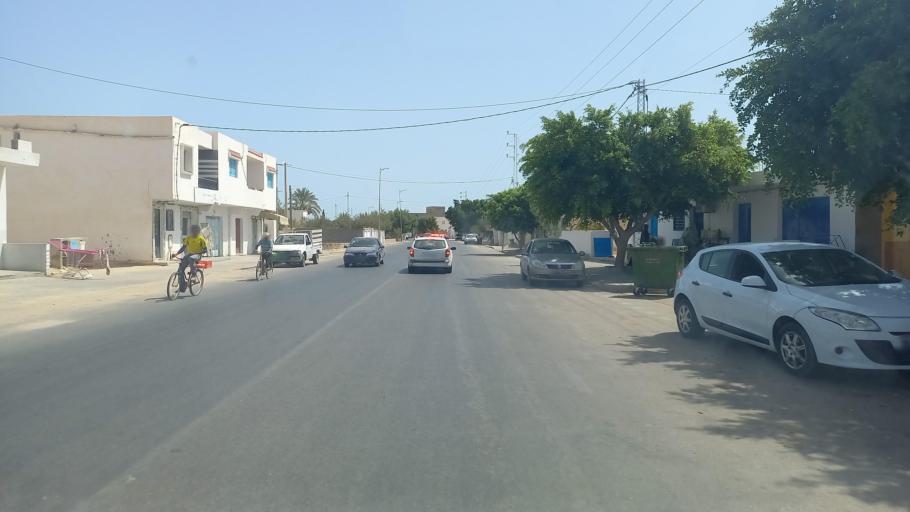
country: TN
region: Madanin
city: Zarzis
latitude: 33.4925
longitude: 11.0748
